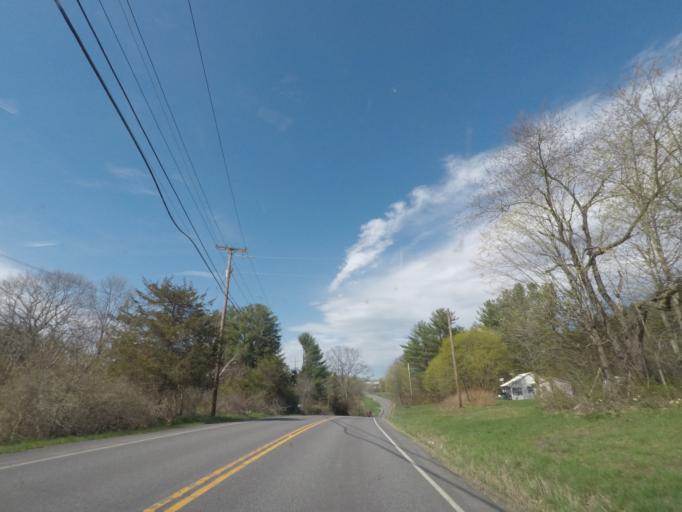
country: US
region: New York
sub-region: Greene County
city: Cairo
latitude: 42.3940
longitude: -74.0296
